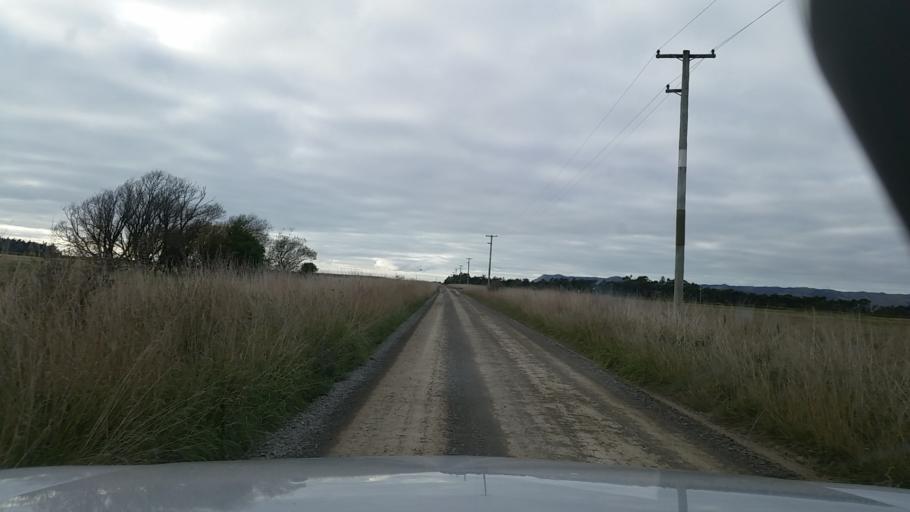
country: NZ
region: Marlborough
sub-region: Marlborough District
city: Blenheim
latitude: -41.5096
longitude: 174.0323
